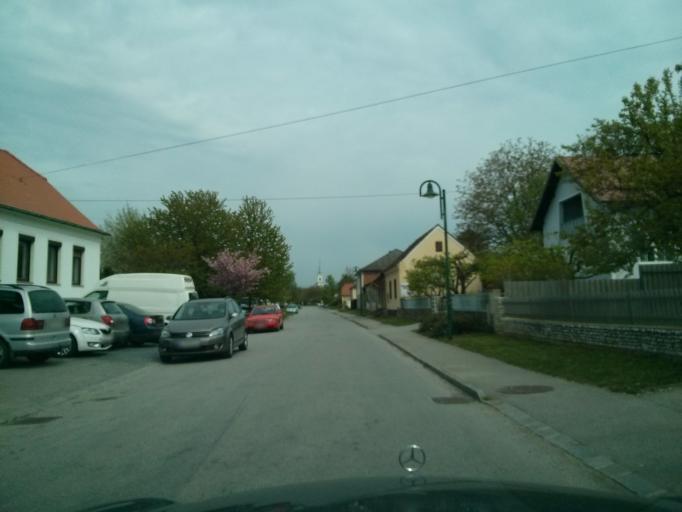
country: AT
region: Burgenland
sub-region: Politischer Bezirk Oberwart
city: Bad Tatzmannsdorf
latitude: 47.3182
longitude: 16.2045
